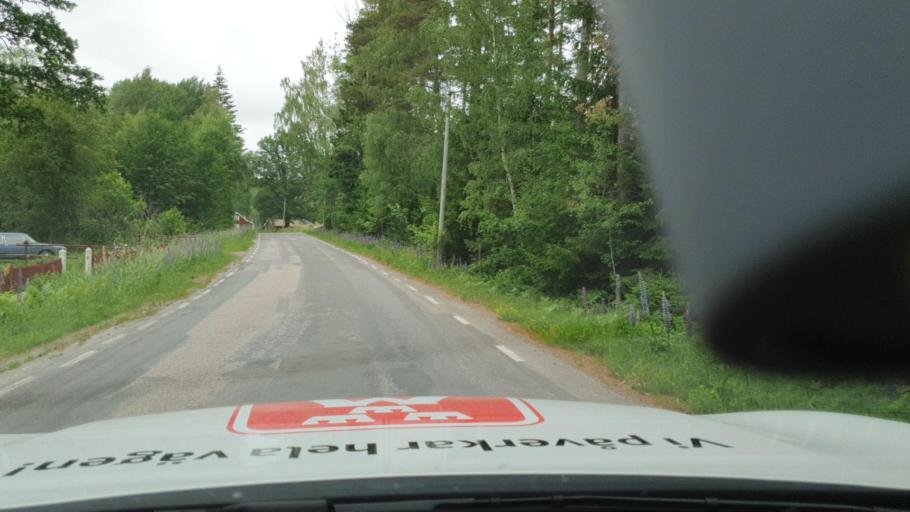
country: SE
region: Vaestra Goetaland
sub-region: Tibro Kommun
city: Tibro
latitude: 58.3660
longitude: 14.2018
